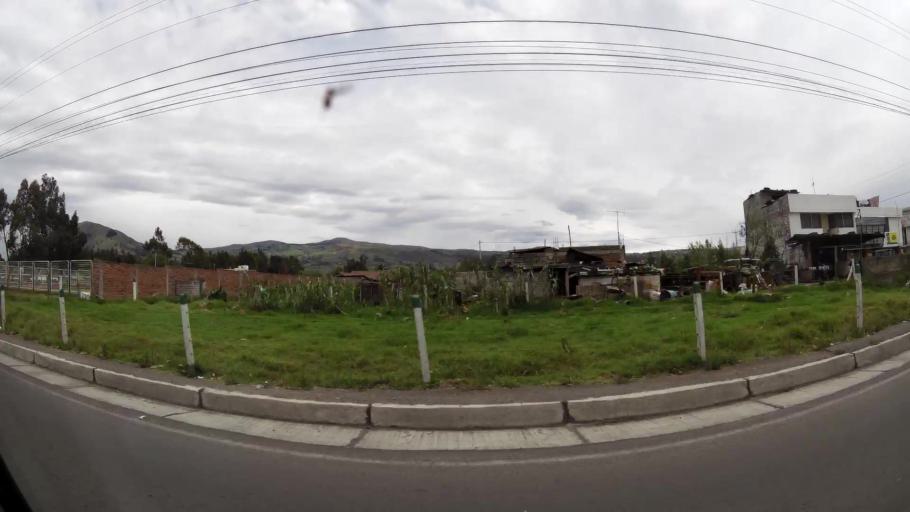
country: EC
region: Cotopaxi
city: San Miguel de Salcedo
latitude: -1.0166
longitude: -78.5922
